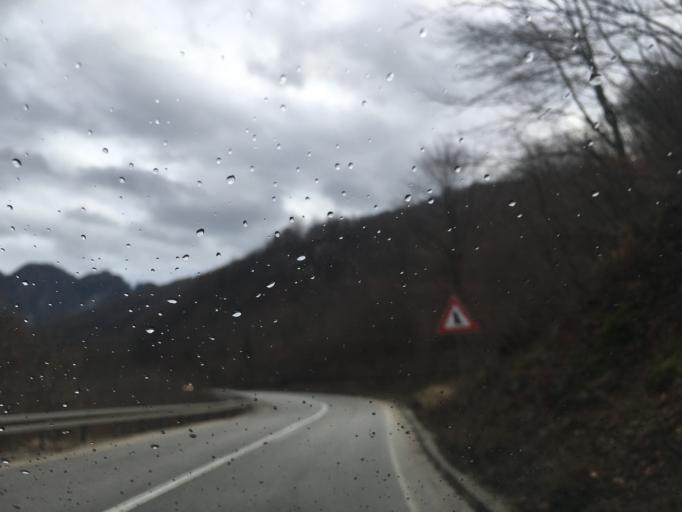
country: RS
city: Sokolovo Brdo
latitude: 43.2003
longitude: 19.7625
